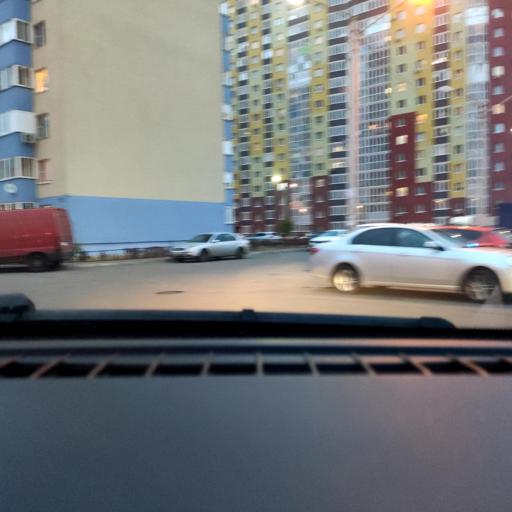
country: RU
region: Voronezj
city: Somovo
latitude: 51.7401
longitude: 39.3137
